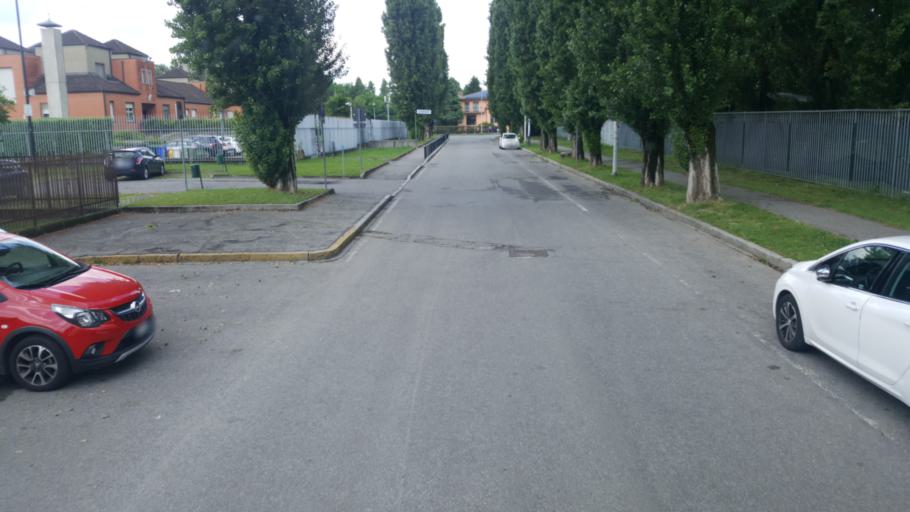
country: IT
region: Lombardy
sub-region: Citta metropolitana di Milano
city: Melzo
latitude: 45.4949
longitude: 9.4166
